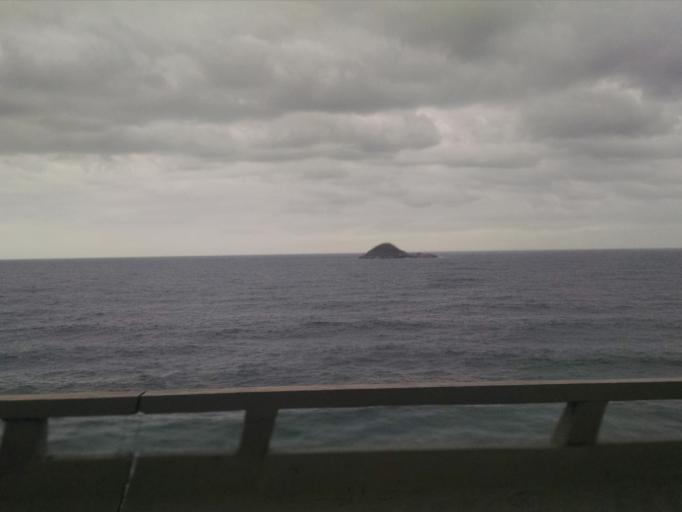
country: BR
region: Rio de Janeiro
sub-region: Rio De Janeiro
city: Rio de Janeiro
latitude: -23.0058
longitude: -43.2806
